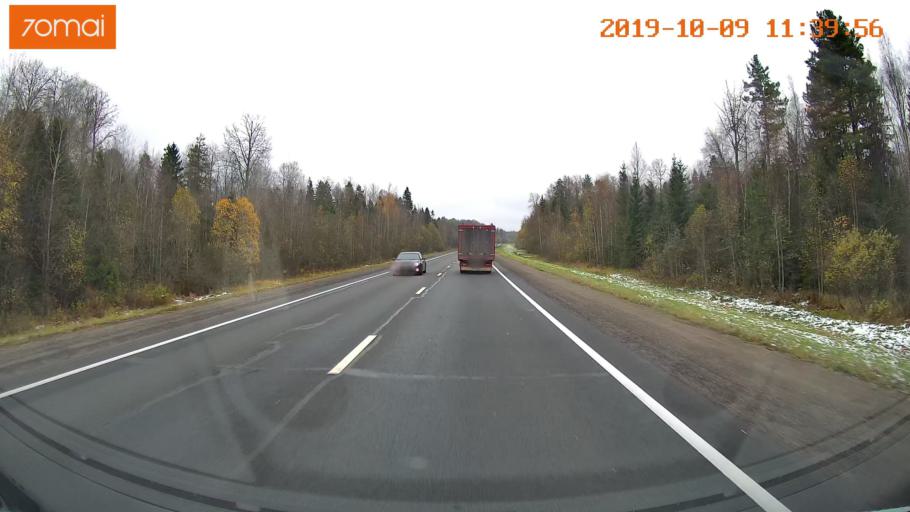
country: RU
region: Vologda
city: Gryazovets
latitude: 58.9501
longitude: 40.1708
